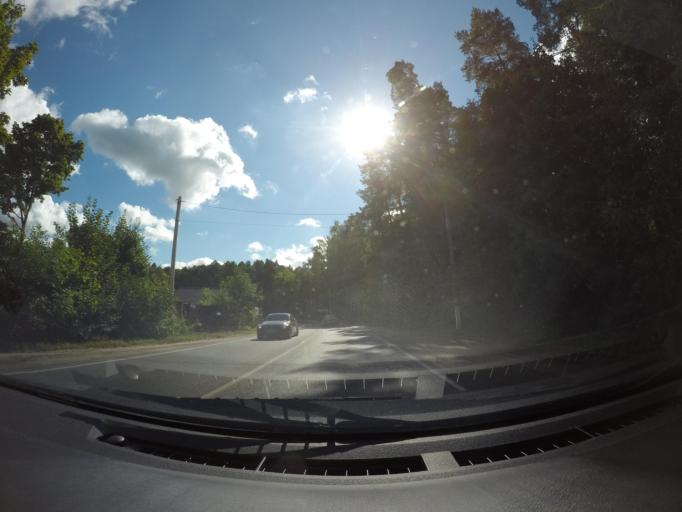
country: RU
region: Moskovskaya
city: Kratovo
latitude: 55.6037
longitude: 38.1511
